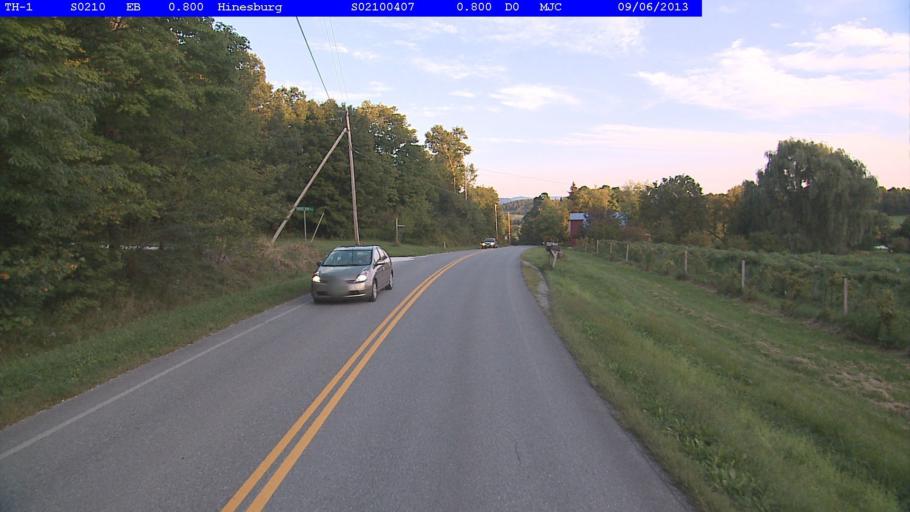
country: US
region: Vermont
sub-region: Chittenden County
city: Hinesburg
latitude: 44.3529
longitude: -73.1532
